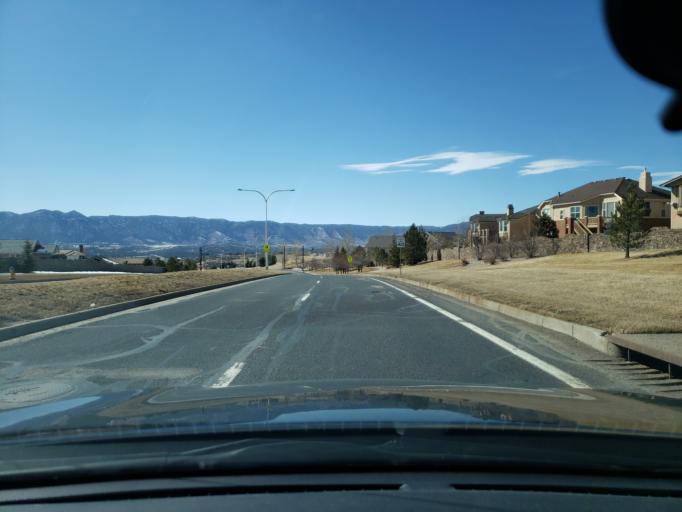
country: US
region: Colorado
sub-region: El Paso County
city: Gleneagle
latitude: 39.0300
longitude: -104.7874
